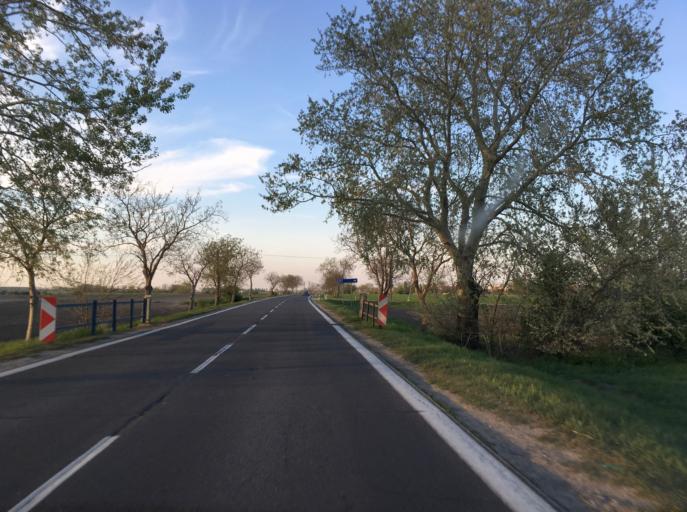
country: SK
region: Trnavsky
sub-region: Okres Dunajska Streda
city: Velky Meder
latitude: 47.8465
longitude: 17.7323
